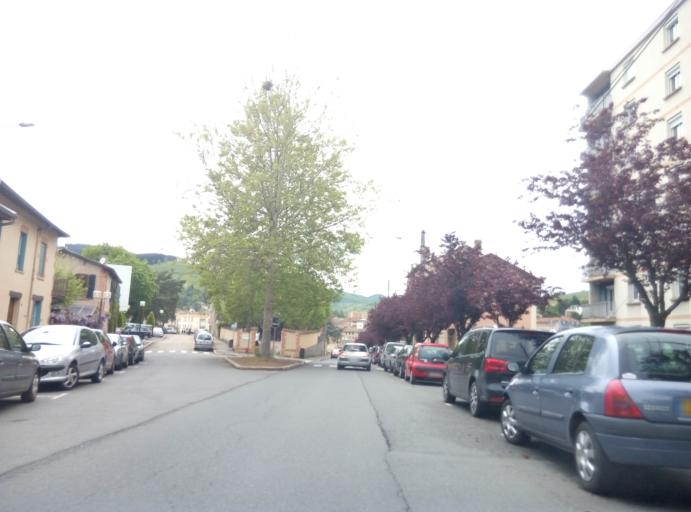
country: FR
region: Rhone-Alpes
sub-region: Departement du Rhone
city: Tarare
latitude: 45.8909
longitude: 4.4398
